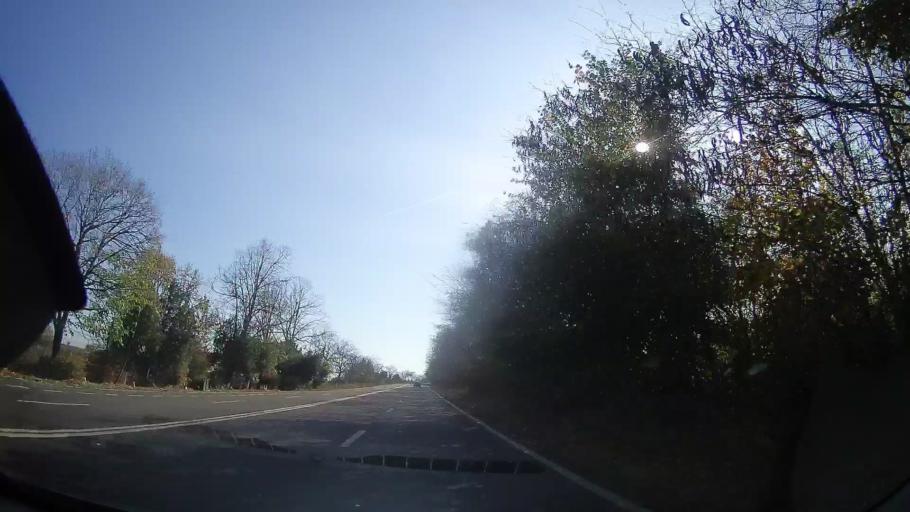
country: RO
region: Constanta
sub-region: Comuna Douazeci si Trei August
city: Douazeci si Trei August
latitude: 43.8895
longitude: 28.5727
